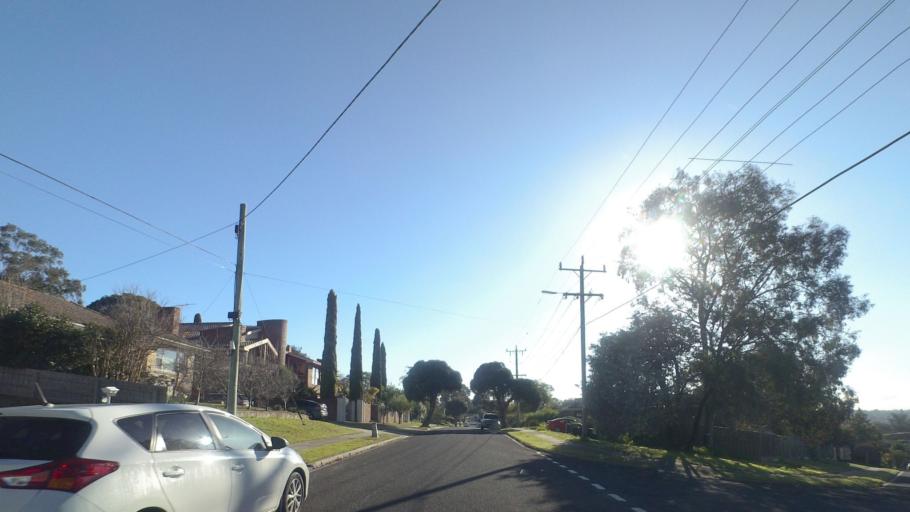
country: AU
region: Victoria
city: Macleod
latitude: -37.7331
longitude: 145.0629
